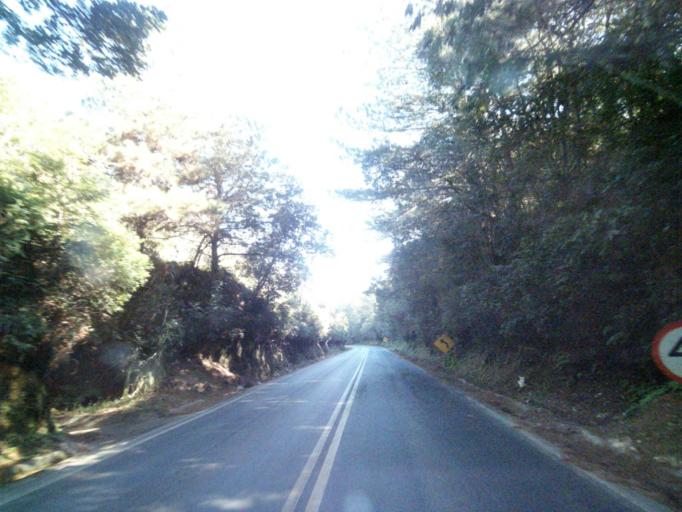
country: BR
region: Parana
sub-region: Tibagi
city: Tibagi
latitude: -24.5279
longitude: -50.3914
